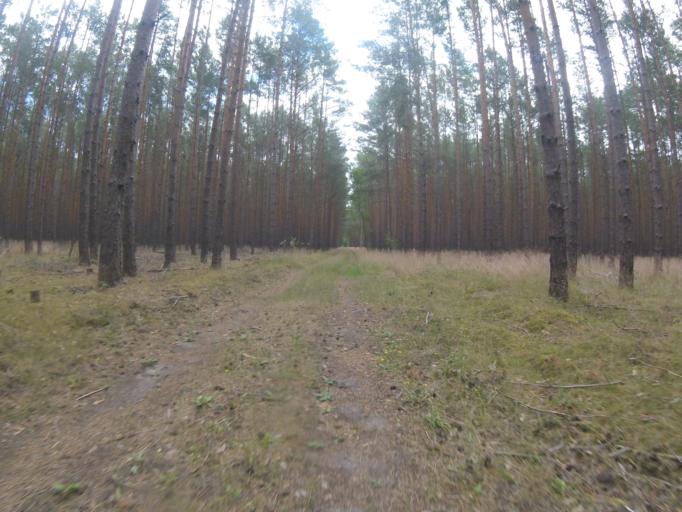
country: DE
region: Brandenburg
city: Bestensee
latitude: 52.2861
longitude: 13.7274
